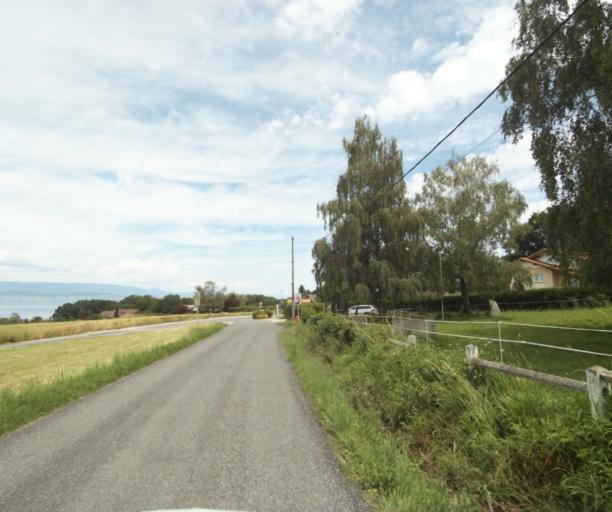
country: FR
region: Rhone-Alpes
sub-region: Departement de la Haute-Savoie
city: Anthy-sur-Leman
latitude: 46.3510
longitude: 6.4093
